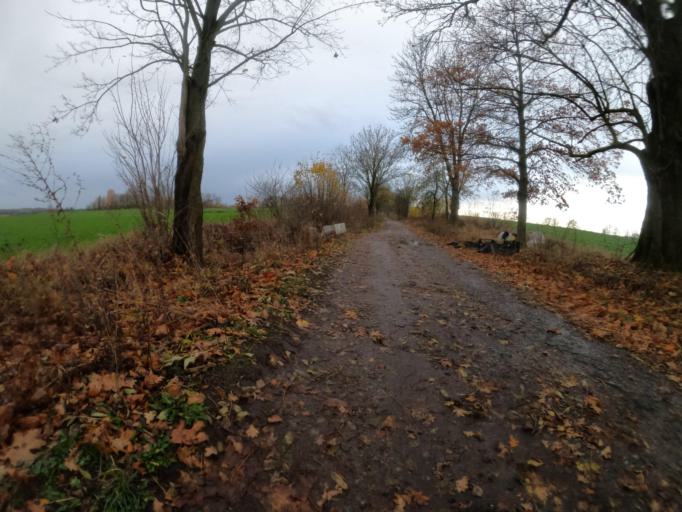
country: PL
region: West Pomeranian Voivodeship
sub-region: Powiat walecki
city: Tuczno
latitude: 53.2075
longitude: 16.2161
